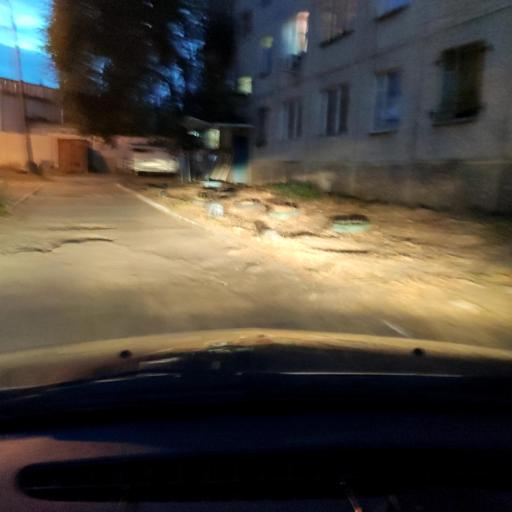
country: RU
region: Voronezj
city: Pridonskoy
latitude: 51.6733
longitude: 39.1030
